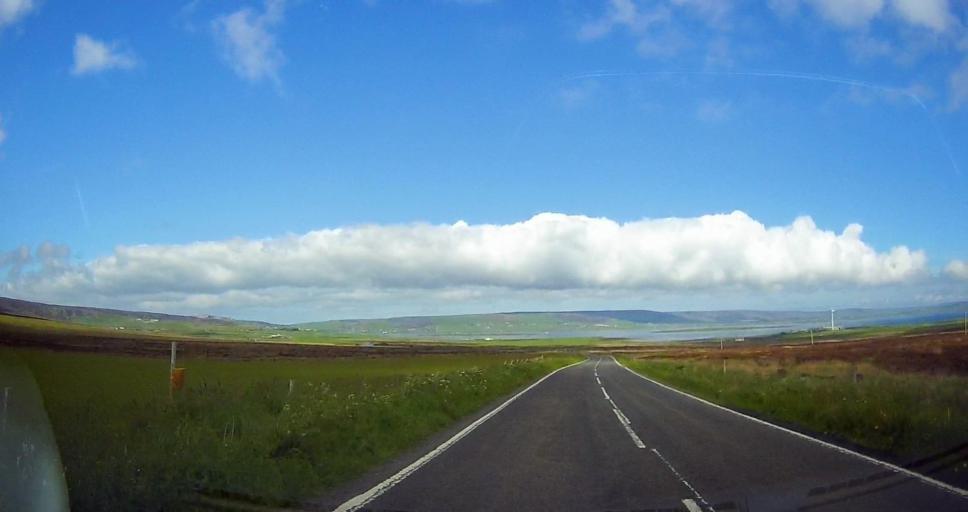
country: GB
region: Scotland
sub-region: Orkney Islands
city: Orkney
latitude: 58.9841
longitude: -3.0451
